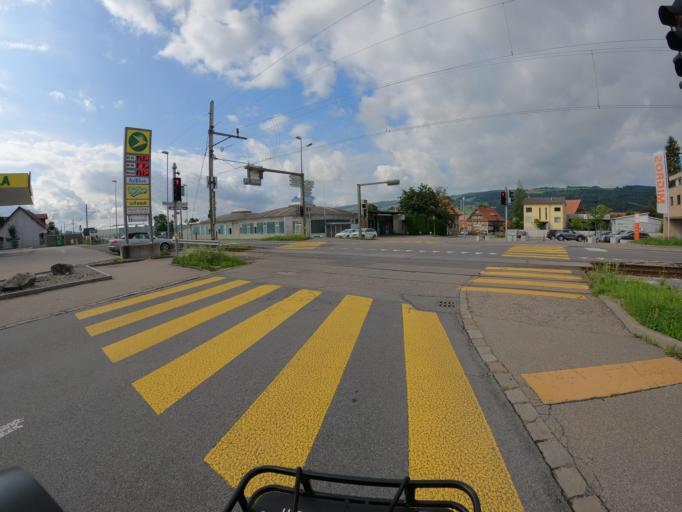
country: CH
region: Lucerne
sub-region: Hochdorf District
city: Hitzkirch
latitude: 47.2222
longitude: 8.2527
